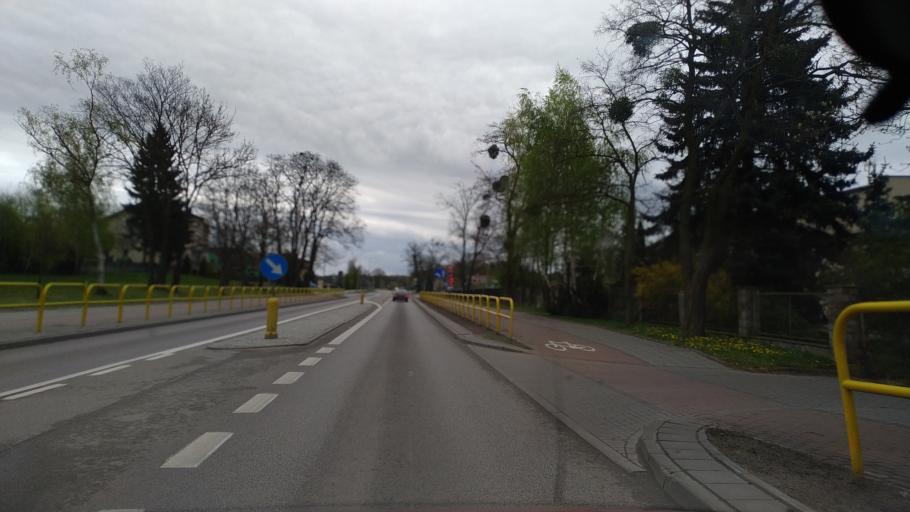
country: PL
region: Pomeranian Voivodeship
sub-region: Powiat starogardzki
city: Starogard Gdanski
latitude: 53.9715
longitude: 18.5403
